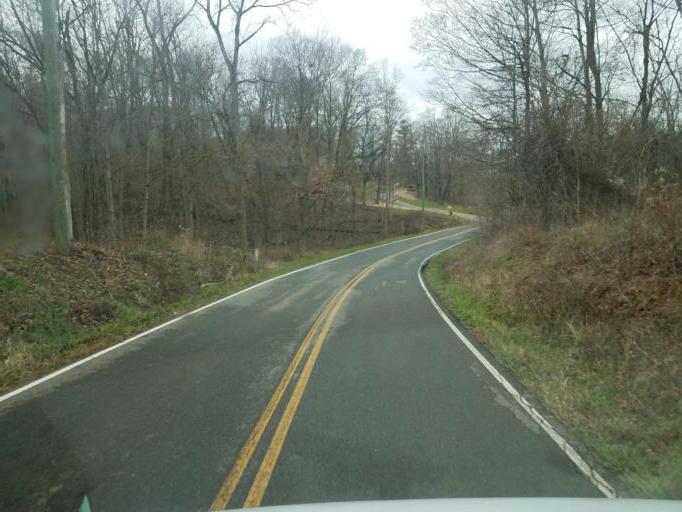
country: US
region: Ohio
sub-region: Licking County
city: Johnstown
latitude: 40.2306
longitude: -82.6466
